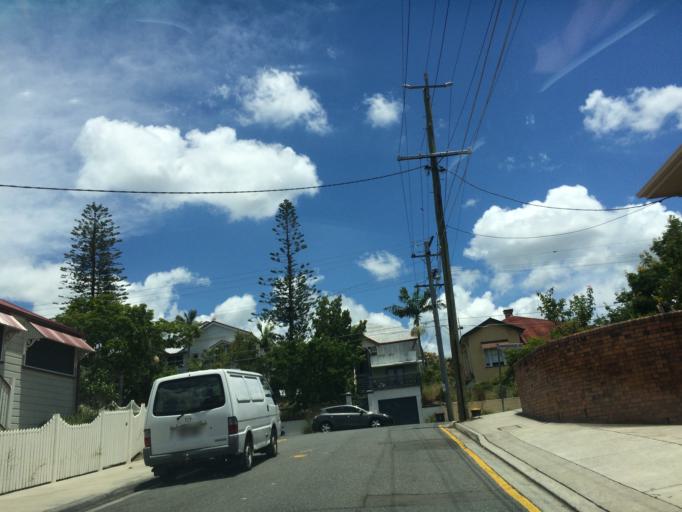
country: AU
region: Queensland
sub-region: Brisbane
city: South Brisbane
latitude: -27.4835
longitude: 153.0072
